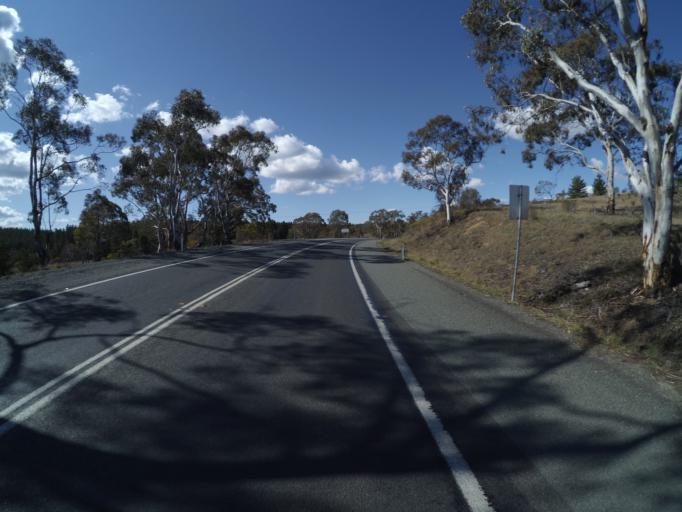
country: AU
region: New South Wales
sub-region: Queanbeyan
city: Queanbeyan
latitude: -35.3375
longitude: 149.2877
